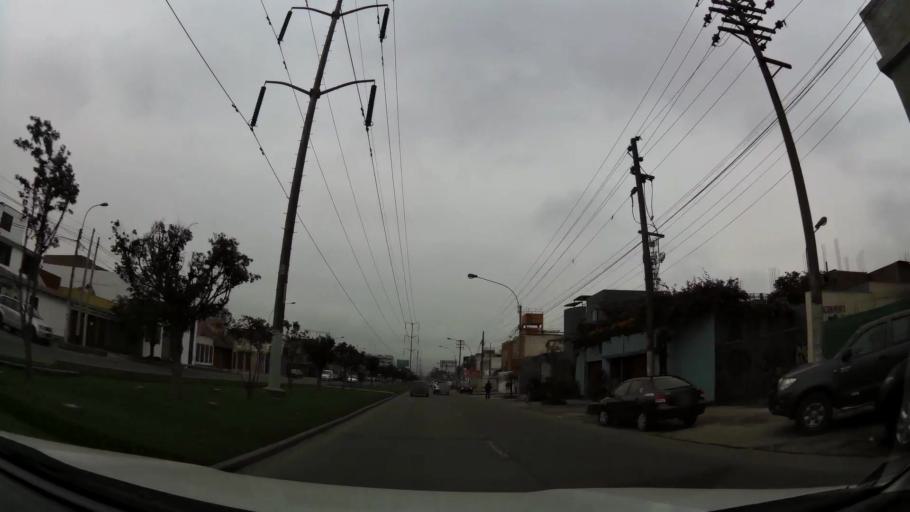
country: PE
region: Lima
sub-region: Lima
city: La Molina
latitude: -12.0648
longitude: -76.9599
